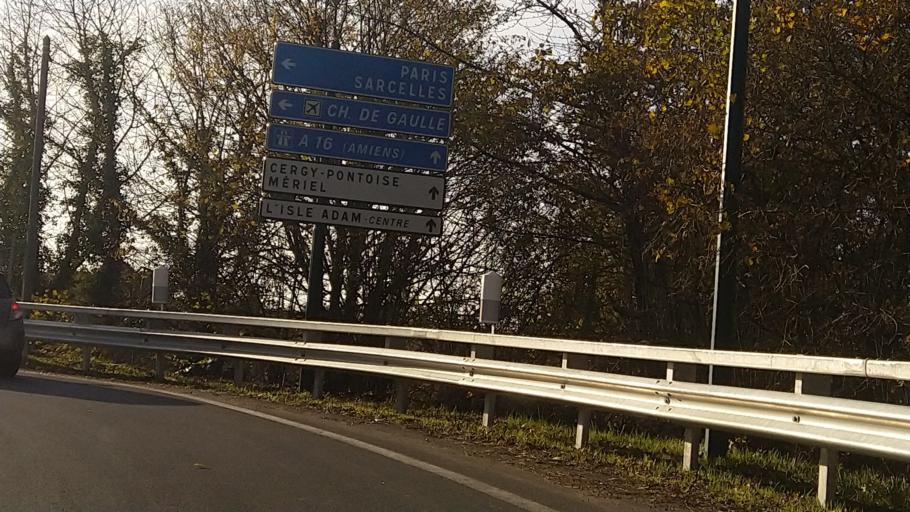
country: FR
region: Ile-de-France
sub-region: Departement du Val-d'Oise
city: Mours
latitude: 49.1018
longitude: 2.2761
